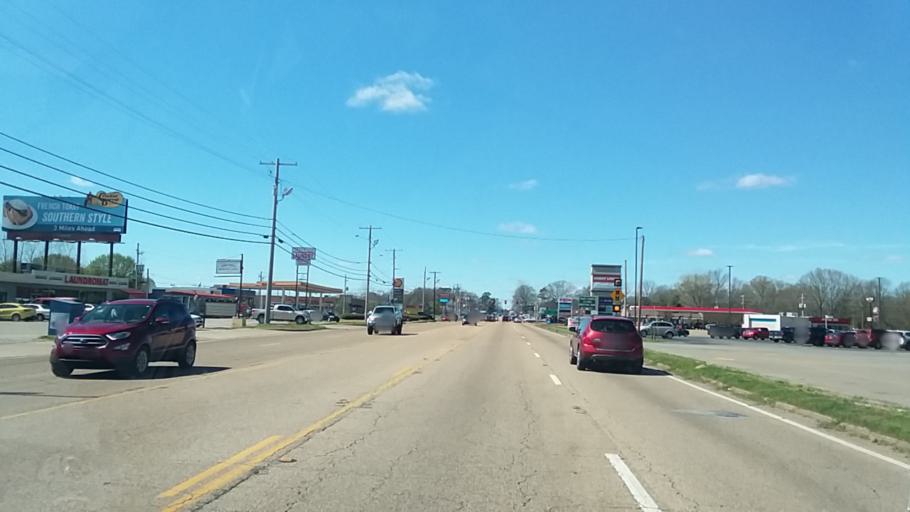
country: US
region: Mississippi
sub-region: Alcorn County
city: Corinth
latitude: 34.9128
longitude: -88.4990
